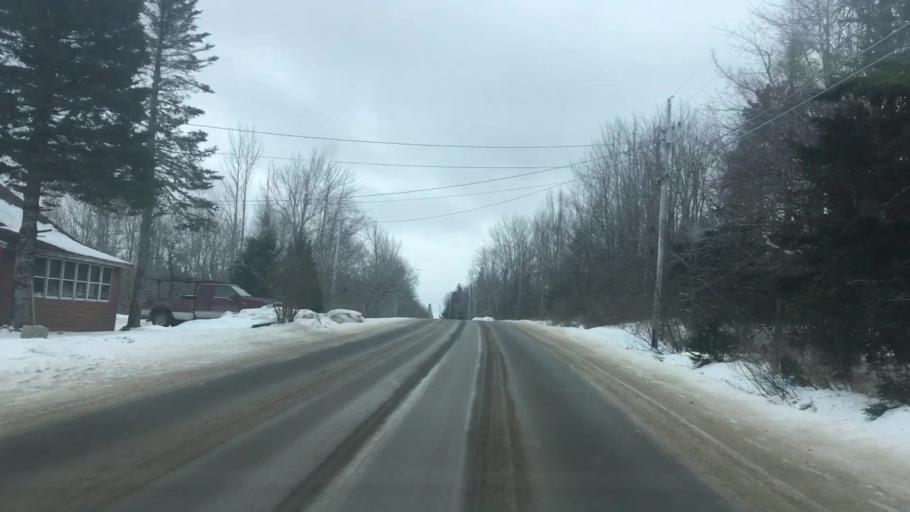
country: US
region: Maine
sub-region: Washington County
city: East Machias
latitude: 44.9874
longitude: -67.4586
